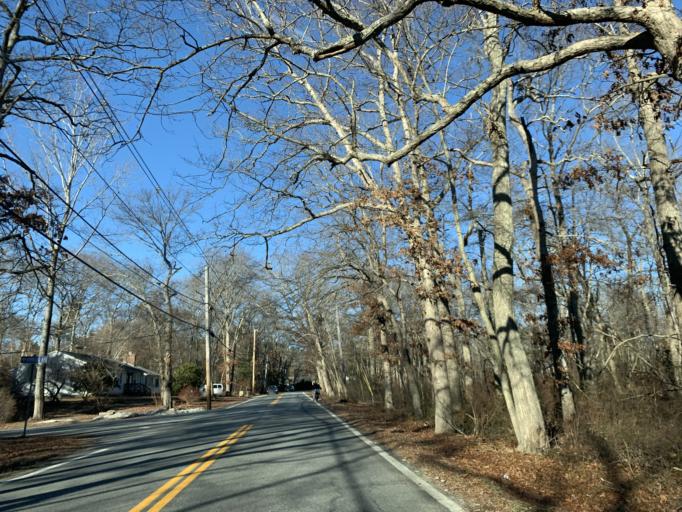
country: US
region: Rhode Island
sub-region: Washington County
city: Exeter
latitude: 41.5670
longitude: -71.5366
